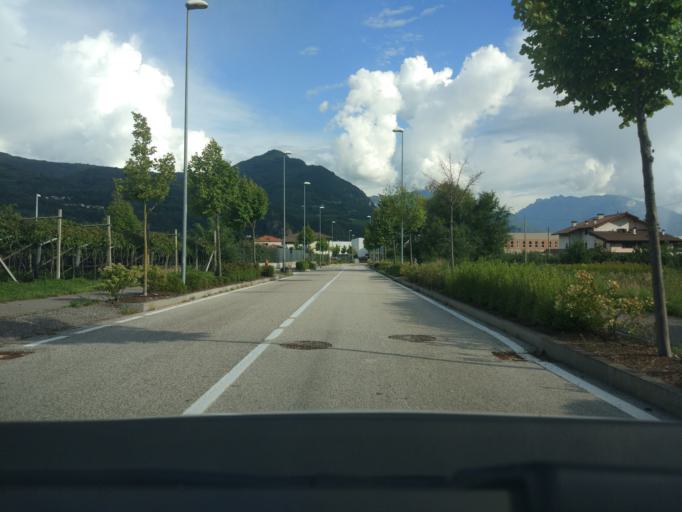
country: IT
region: Trentino-Alto Adige
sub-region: Provincia di Trento
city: Lavis
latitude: 46.1263
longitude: 11.0975
